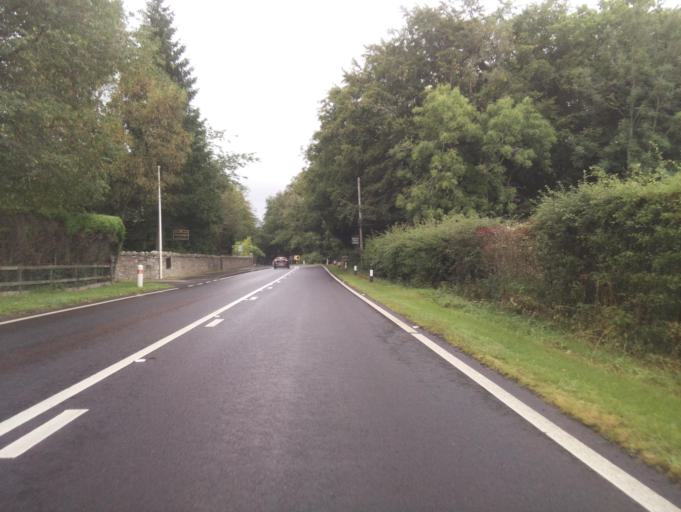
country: GB
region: Scotland
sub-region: The Scottish Borders
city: Jedburgh
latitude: 55.3977
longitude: -2.4990
